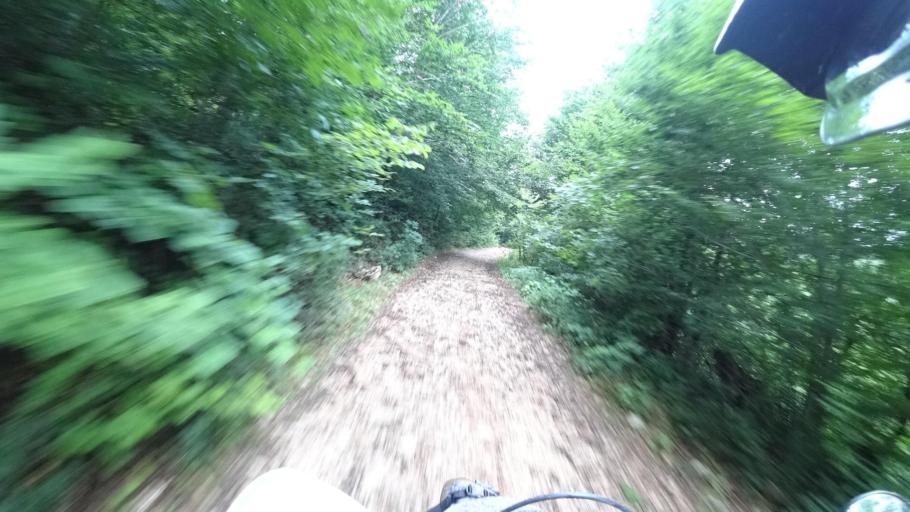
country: HR
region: Licko-Senjska
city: Jezerce
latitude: 44.7530
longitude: 15.4795
